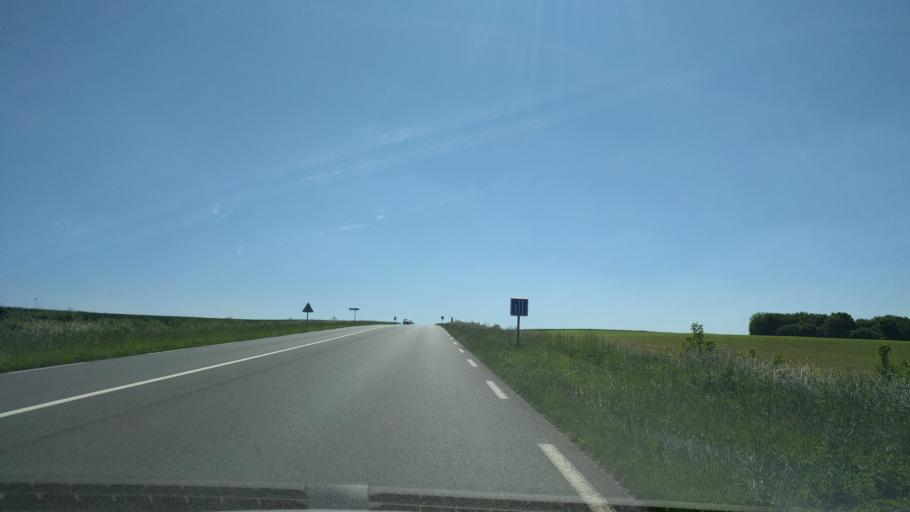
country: FR
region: Picardie
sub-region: Departement de la Somme
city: Peronne
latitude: 49.8917
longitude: 2.9191
